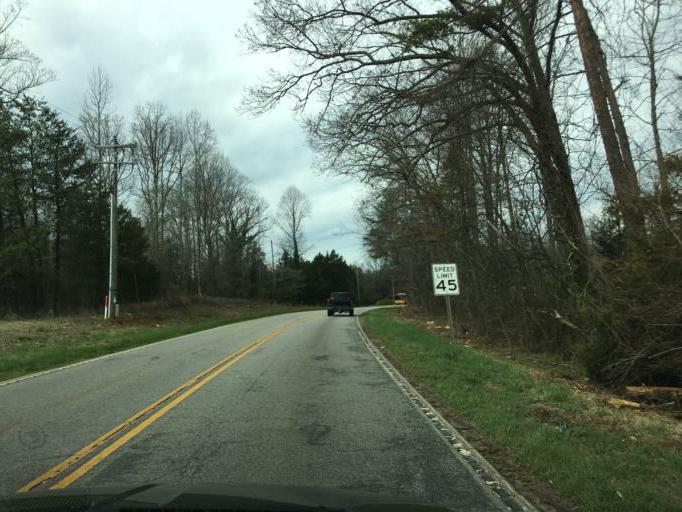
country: US
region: South Carolina
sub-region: Anderson County
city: Piedmont
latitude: 34.7004
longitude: -82.4294
